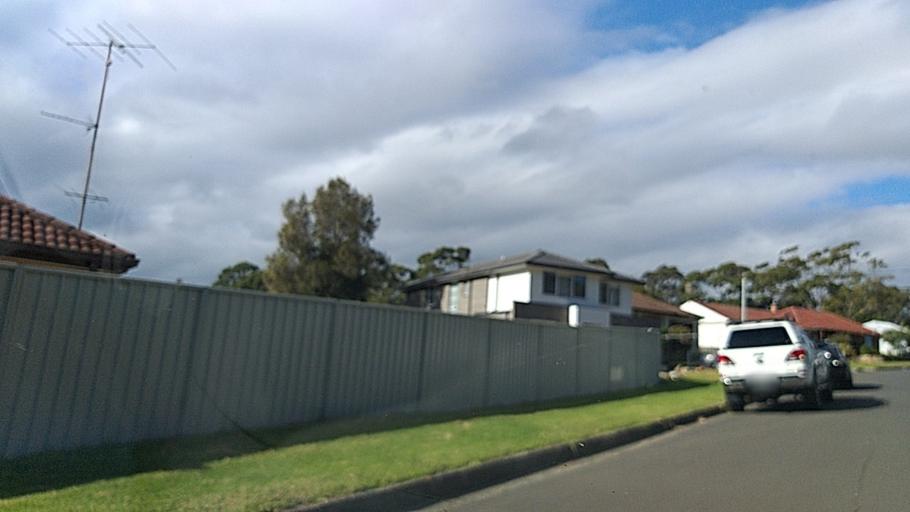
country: AU
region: New South Wales
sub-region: Wollongong
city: Mount Ousley
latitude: -34.3964
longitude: 150.8803
